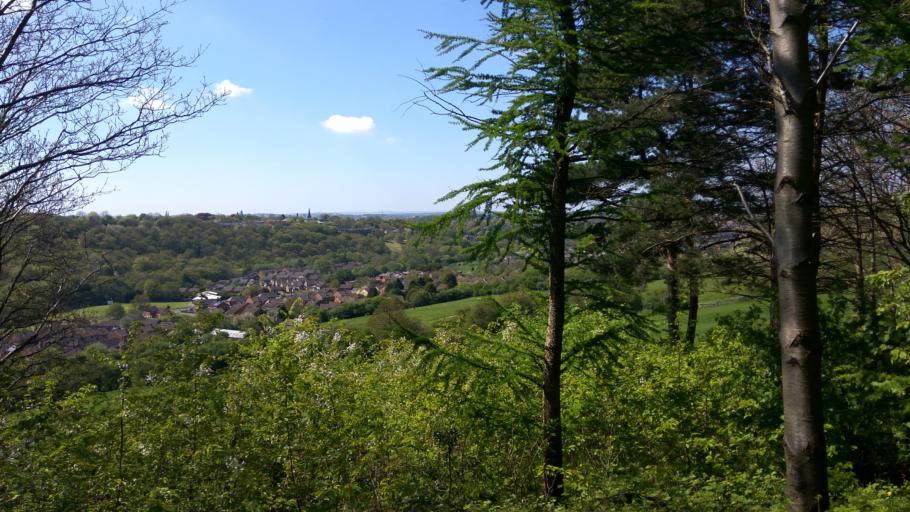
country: GB
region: England
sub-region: City and Borough of Leeds
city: Chapel Allerton
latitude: 53.8242
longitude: -1.5521
